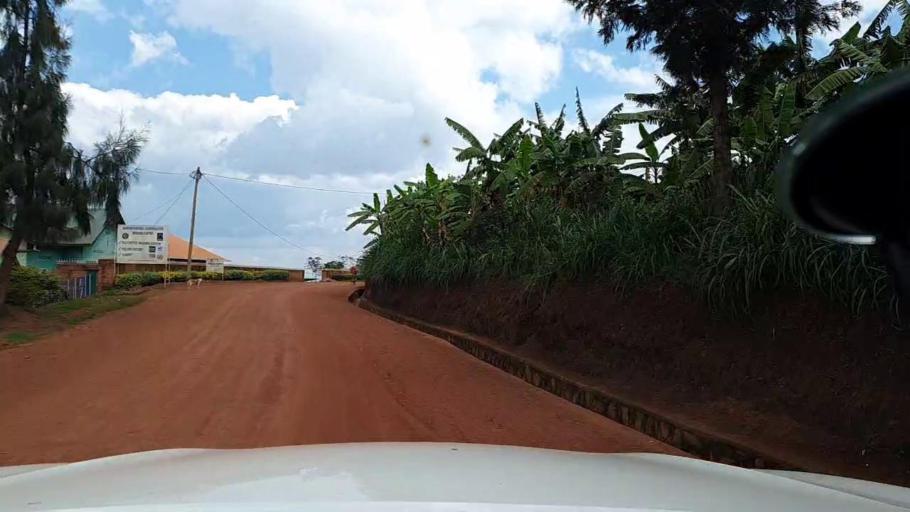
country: RW
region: Kigali
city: Kigali
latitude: -1.8108
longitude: 29.8446
